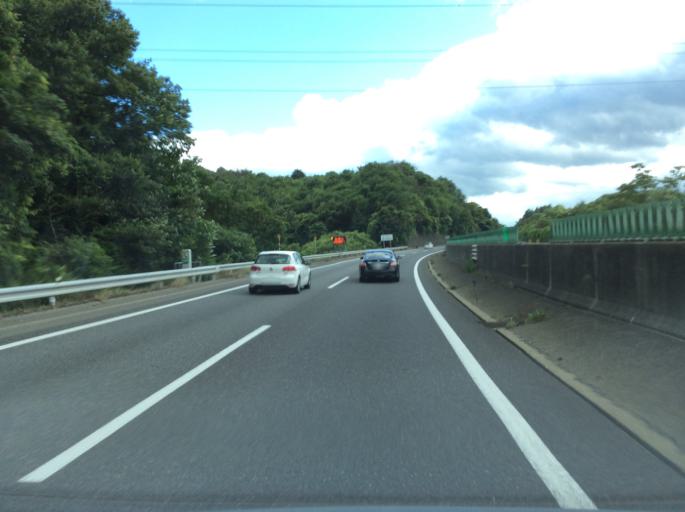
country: JP
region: Fukushima
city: Fukushima-shi
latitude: 37.6687
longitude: 140.4529
